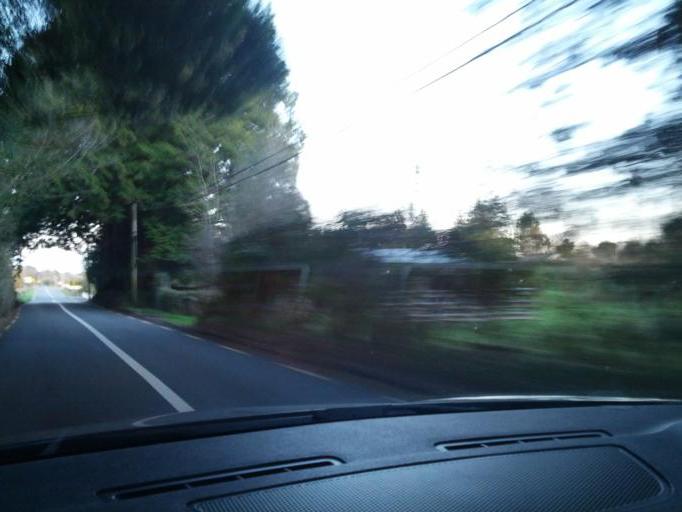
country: IE
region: Connaught
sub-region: Roscommon
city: Boyle
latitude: 53.9725
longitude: -8.3334
